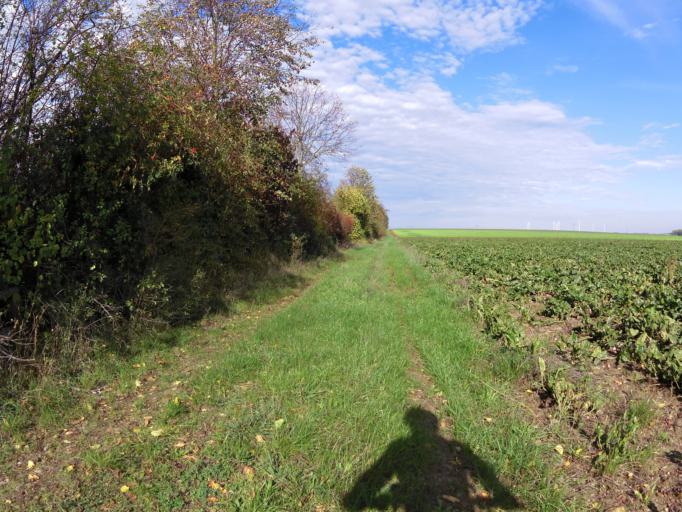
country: DE
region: Bavaria
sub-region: Regierungsbezirk Unterfranken
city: Frickenhausen
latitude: 49.7127
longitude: 10.0732
